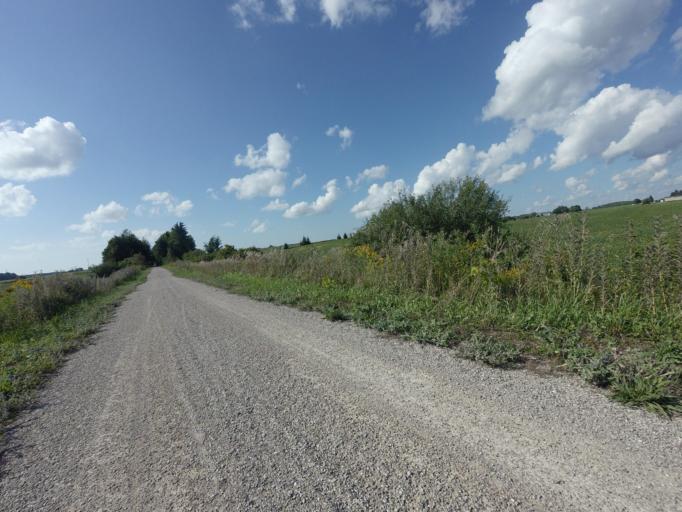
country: CA
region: Ontario
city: Goderich
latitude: 43.7562
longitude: -81.5139
